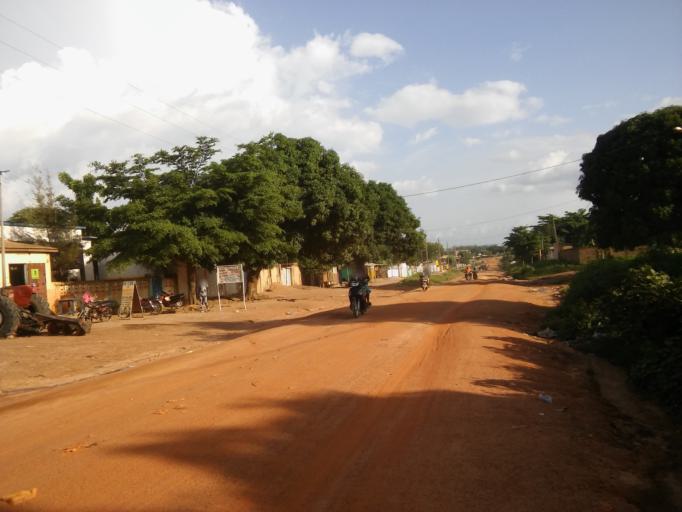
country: BJ
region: Borgou
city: Parakou
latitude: 9.3582
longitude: 2.6377
